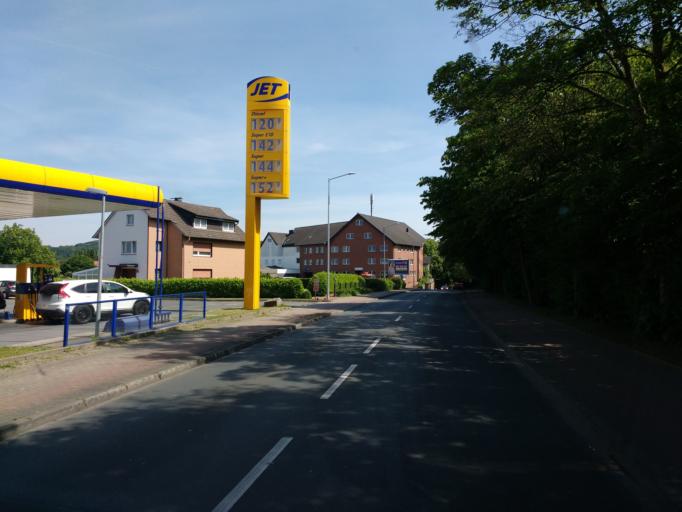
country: DE
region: North Rhine-Westphalia
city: Loehne
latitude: 52.1611
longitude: 8.6661
